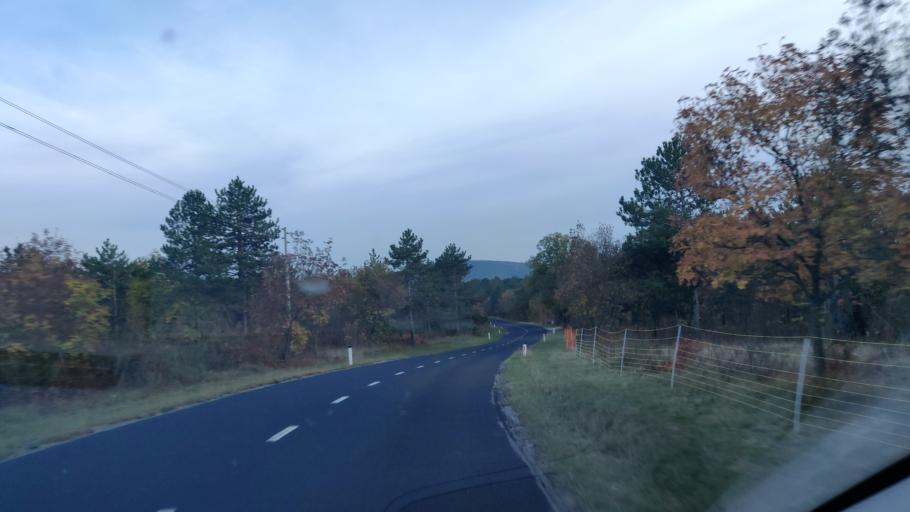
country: SI
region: Sezana
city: Sezana
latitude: 45.7505
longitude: 13.9230
